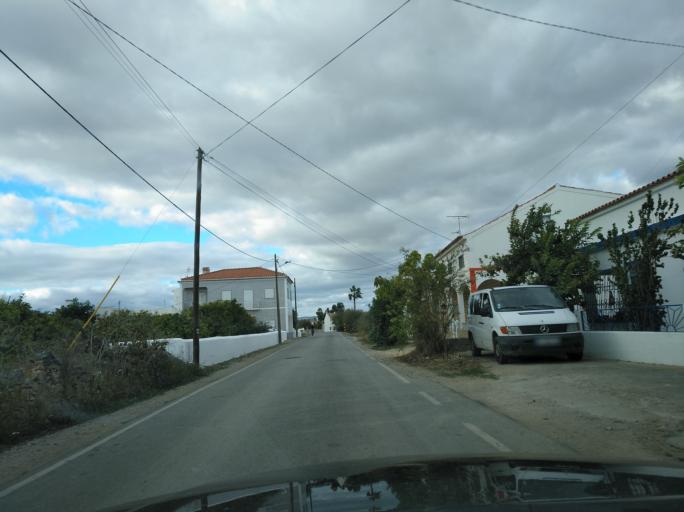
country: PT
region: Faro
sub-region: Tavira
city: Luz
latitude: 37.0965
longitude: -7.7055
